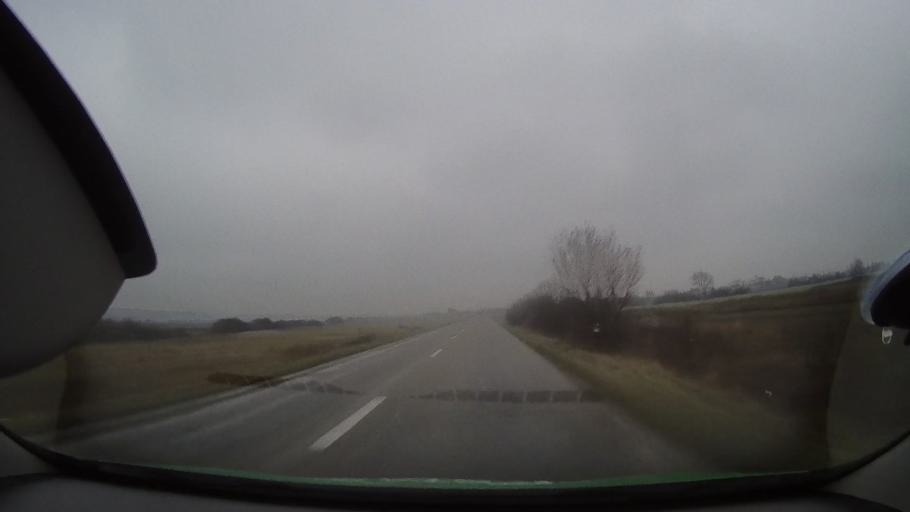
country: RO
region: Bihor
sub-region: Comuna Tinca
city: Gurbediu
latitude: 46.7906
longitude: 21.8480
